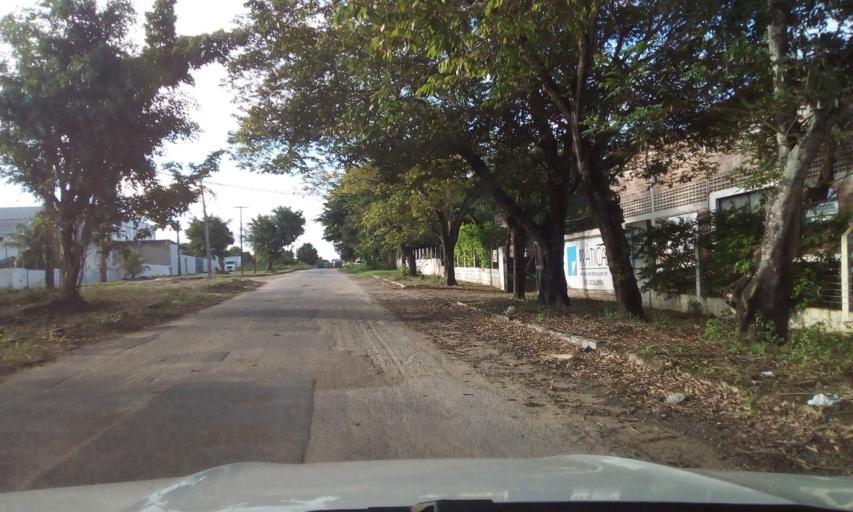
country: BR
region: Paraiba
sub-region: Joao Pessoa
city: Joao Pessoa
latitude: -7.1655
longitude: -34.8228
